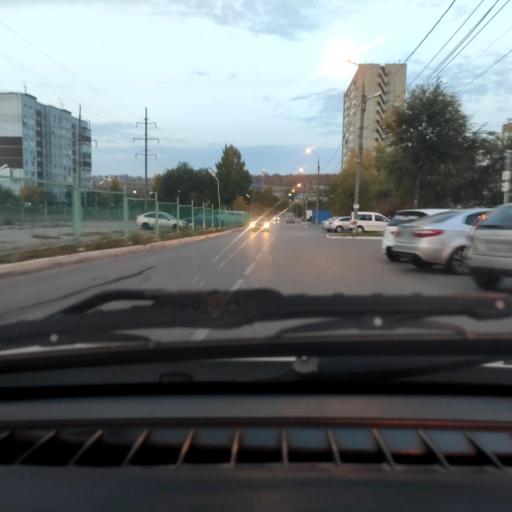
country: RU
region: Samara
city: Zhigulevsk
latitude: 53.4718
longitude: 49.5318
